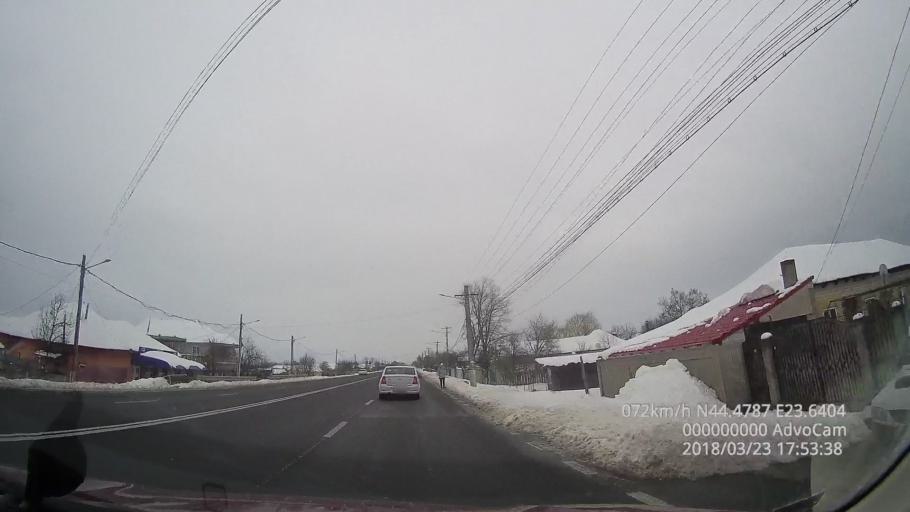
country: RO
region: Dolj
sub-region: Comuna Bradesti
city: Bradesti
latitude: 44.4789
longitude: 23.6402
